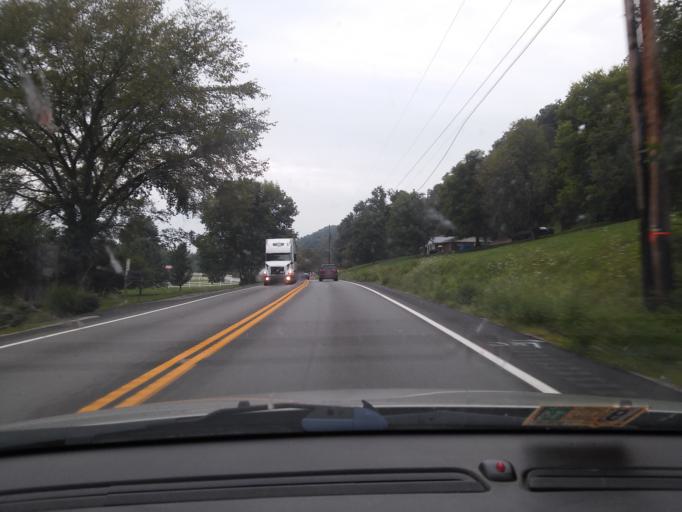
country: US
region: West Virginia
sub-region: Putnam County
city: Buffalo
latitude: 38.5970
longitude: -82.0063
